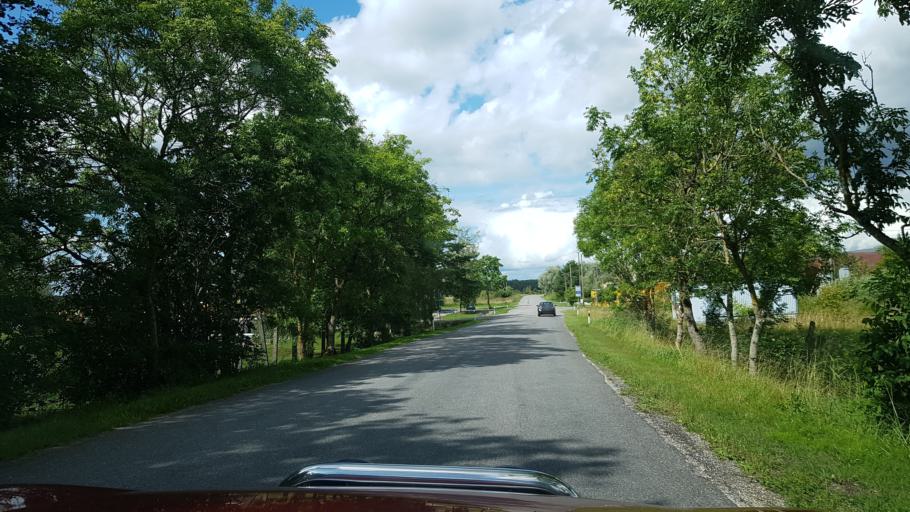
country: EE
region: Laeaene
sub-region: Lihula vald
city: Lihula
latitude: 58.6926
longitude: 23.8363
